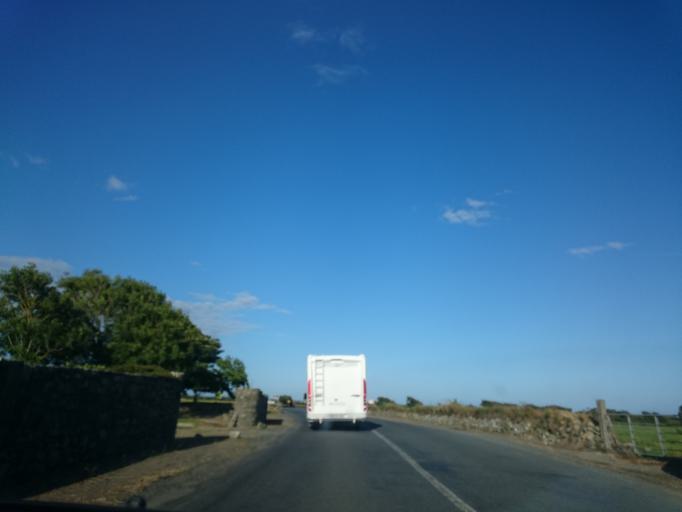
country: IE
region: Leinster
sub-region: Loch Garman
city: Loch Garman
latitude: 52.1875
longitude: -6.5669
